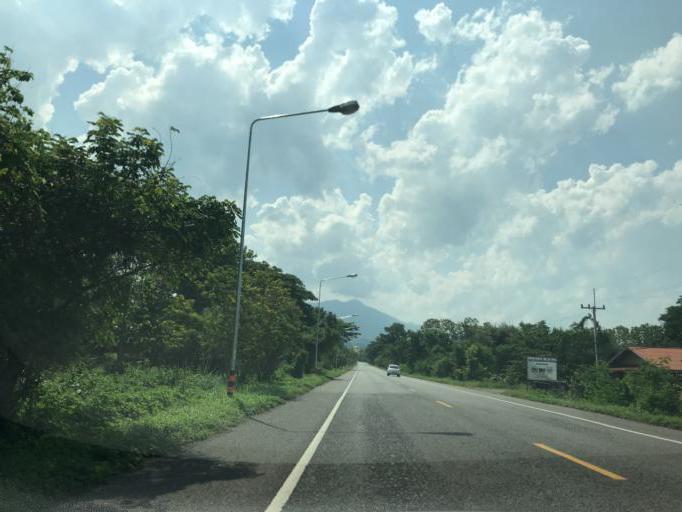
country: TH
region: Phayao
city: Phayao
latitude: 19.0853
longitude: 99.8547
